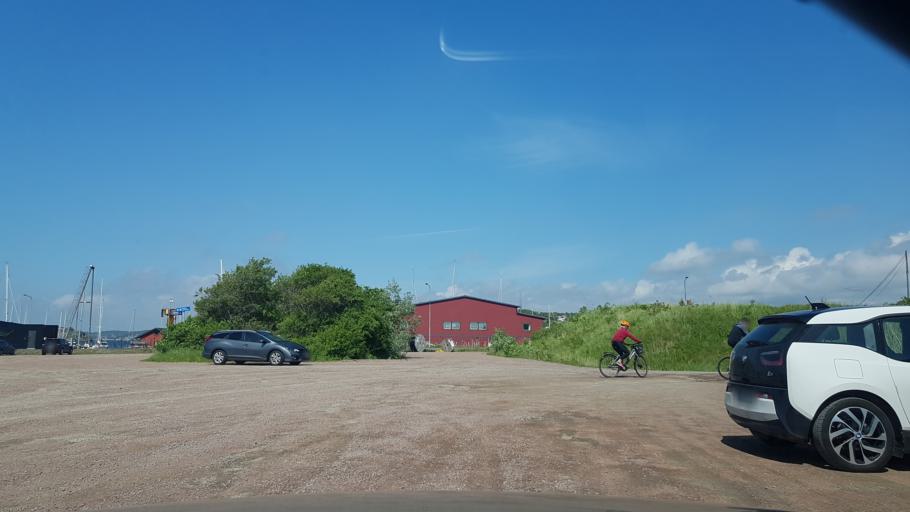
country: SE
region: Vaestra Goetaland
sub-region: Goteborg
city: Billdal
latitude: 57.5961
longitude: 11.9212
